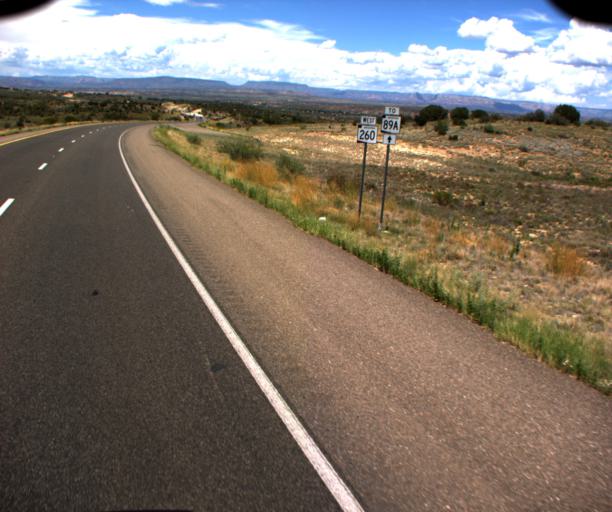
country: US
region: Arizona
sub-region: Yavapai County
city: Verde Village
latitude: 34.6642
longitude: -111.9672
